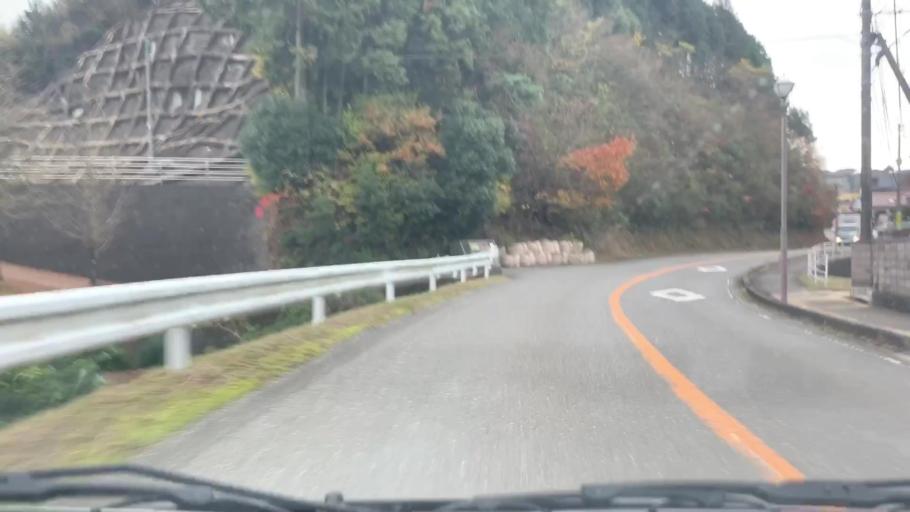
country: JP
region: Saga Prefecture
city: Ureshinomachi-shimojuku
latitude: 33.1044
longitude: 129.9784
